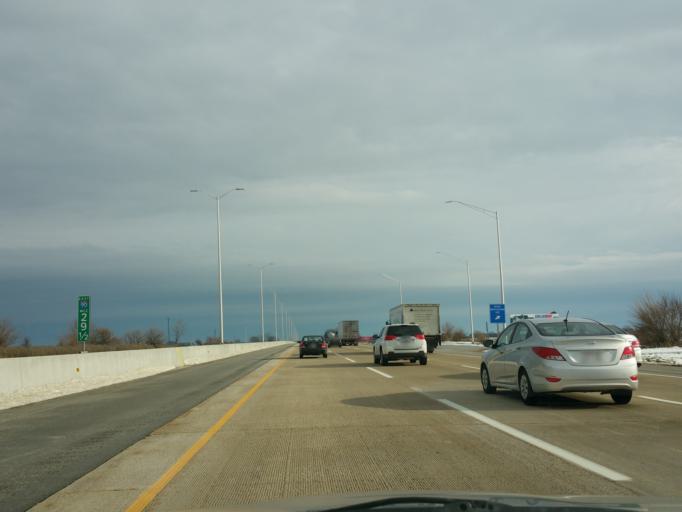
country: US
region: Illinois
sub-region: Boone County
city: Belvidere
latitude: 42.2157
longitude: -88.7372
